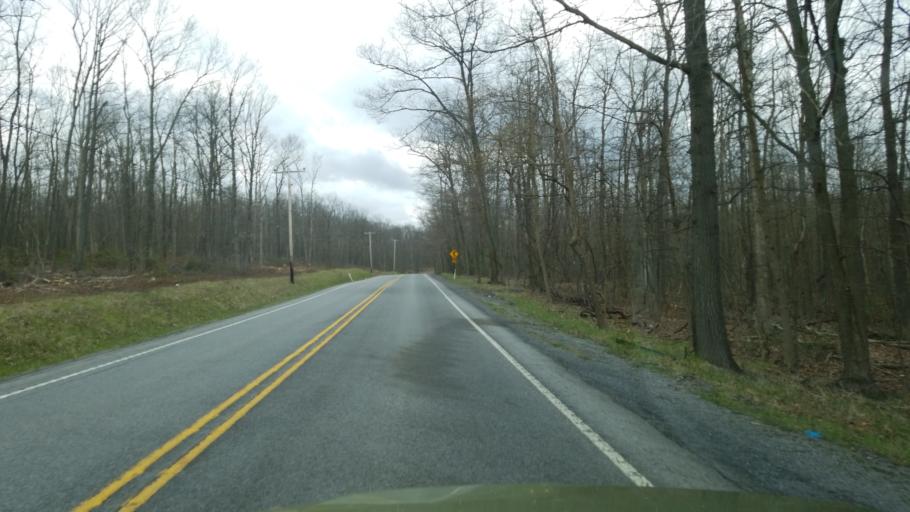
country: US
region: Pennsylvania
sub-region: Blair County
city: Tipton
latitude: 40.7415
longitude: -78.3834
